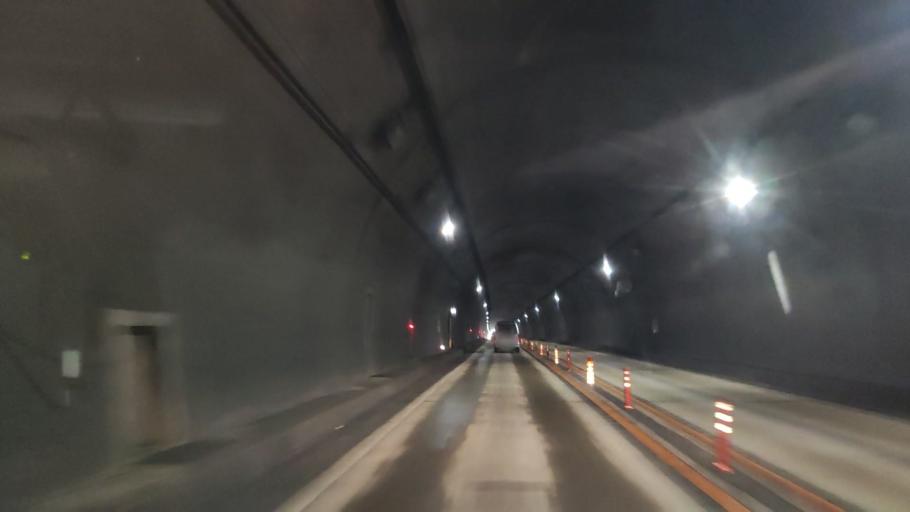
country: JP
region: Tokushima
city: Kamojimacho-jogejima
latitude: 34.1127
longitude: 134.3212
